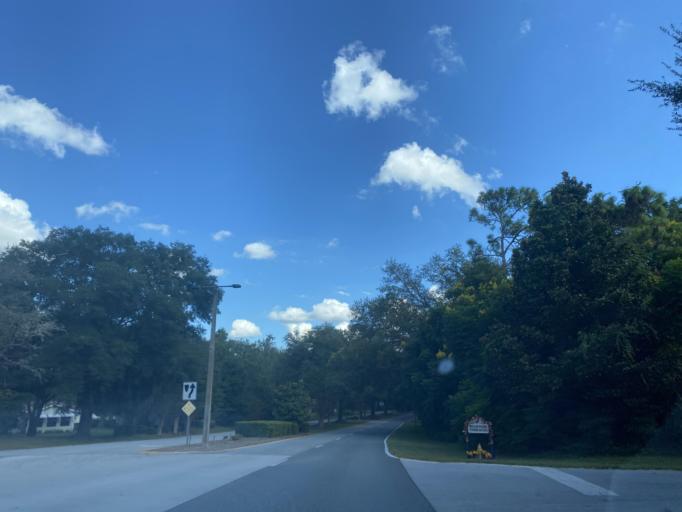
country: US
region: Florida
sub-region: Marion County
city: Ocala
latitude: 29.0571
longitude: -82.2569
